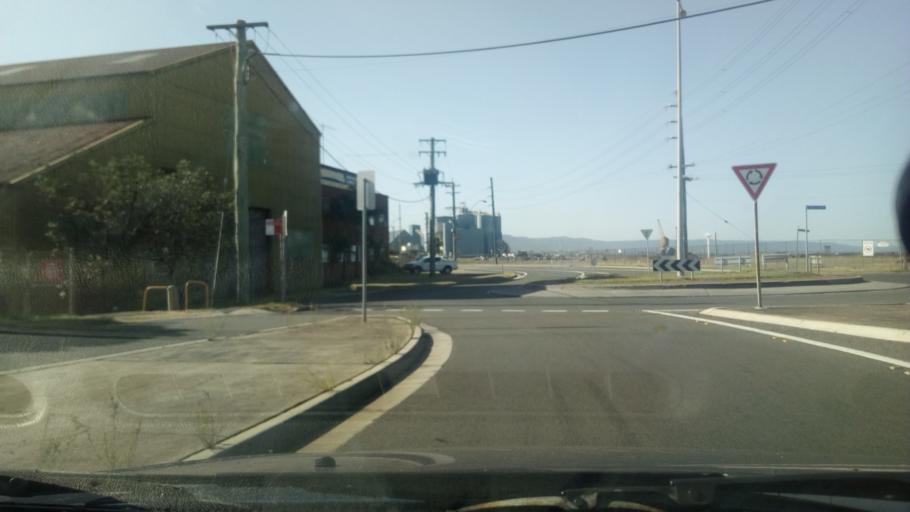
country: AU
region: New South Wales
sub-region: Wollongong
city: Port Kembla
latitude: -34.4772
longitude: 150.9040
